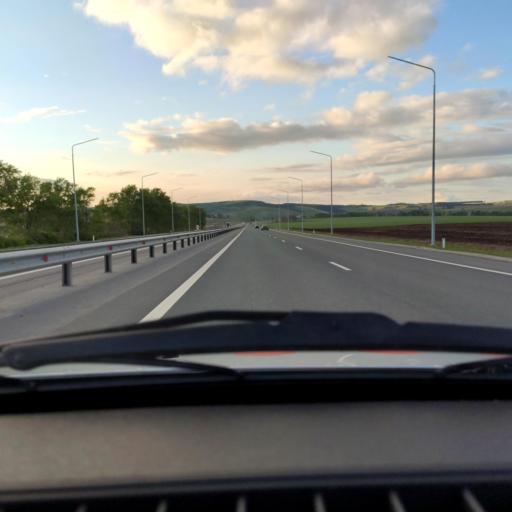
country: RU
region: Bashkortostan
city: Tolbazy
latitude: 54.0513
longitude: 55.8882
